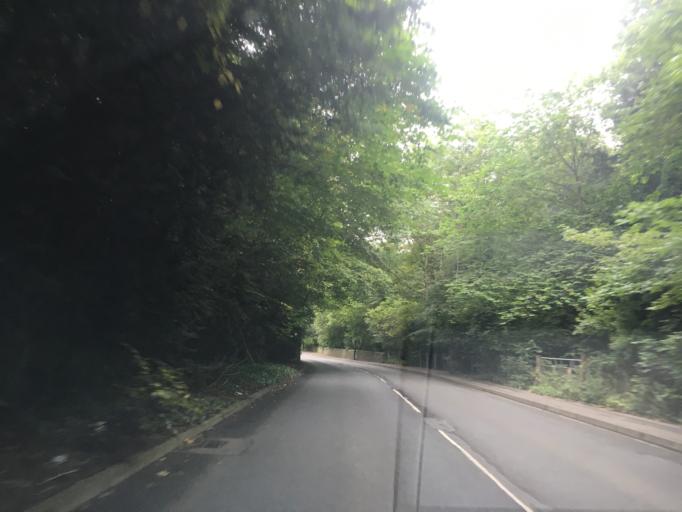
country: GB
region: Scotland
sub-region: Midlothian
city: Dalkeith
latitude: 55.8780
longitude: -3.0690
